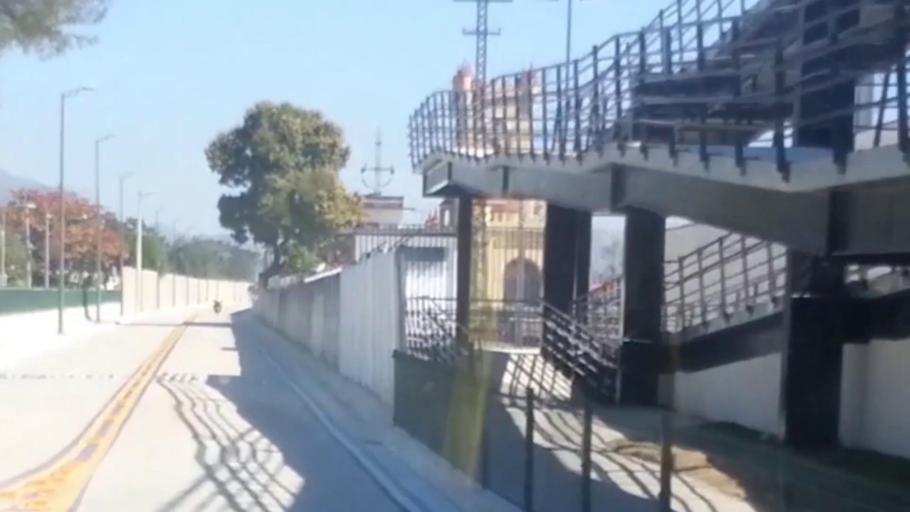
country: BR
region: Rio de Janeiro
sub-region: Nilopolis
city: Nilopolis
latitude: -22.8605
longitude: -43.3974
